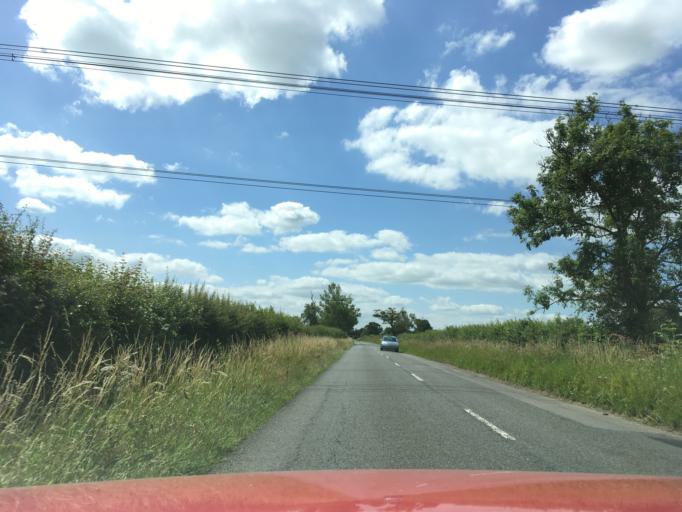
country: GB
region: England
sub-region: Buckinghamshire
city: Winslow
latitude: 51.9254
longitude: -0.8371
